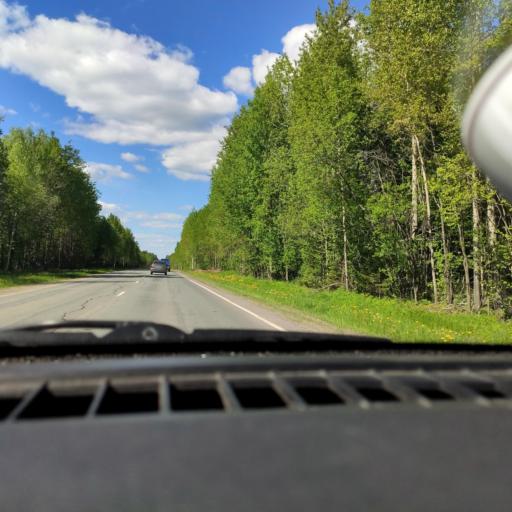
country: RU
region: Perm
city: Polazna
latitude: 58.2704
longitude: 56.1671
